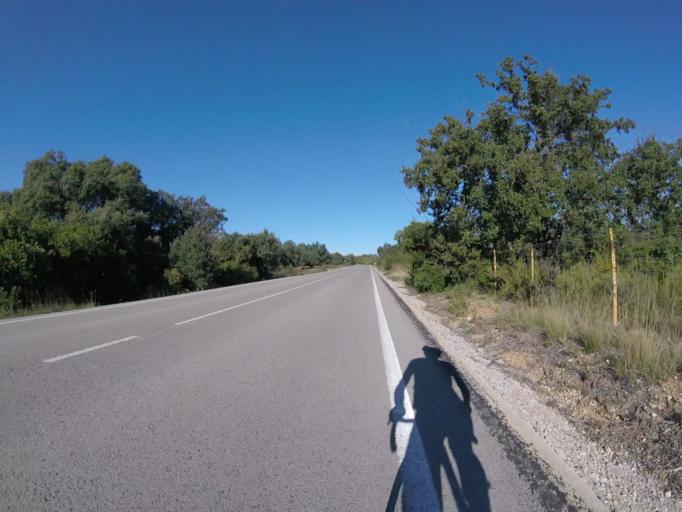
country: ES
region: Valencia
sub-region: Provincia de Castello
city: Cervera del Maestre
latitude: 40.4742
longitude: 0.2306
